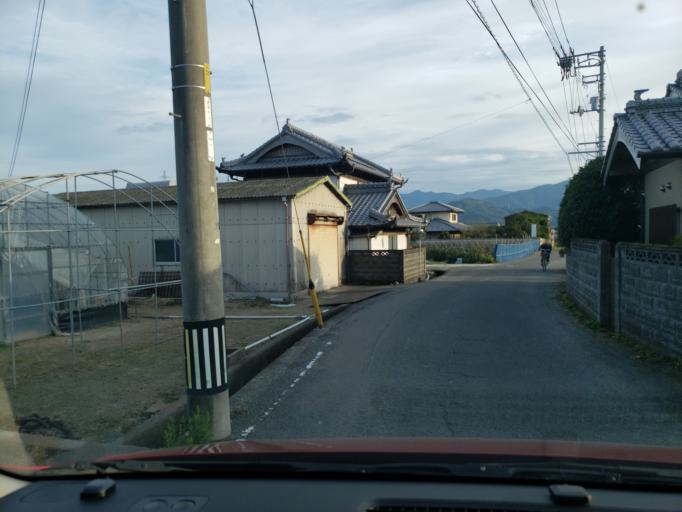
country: JP
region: Tokushima
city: Wakimachi
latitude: 34.0812
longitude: 134.2282
